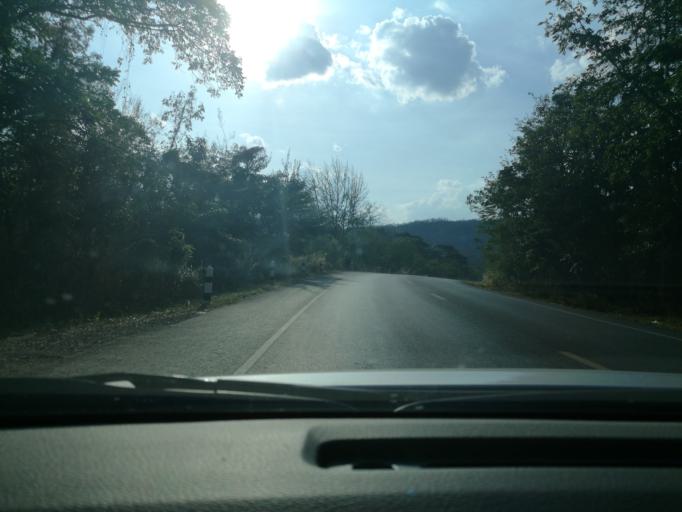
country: TH
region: Phetchabun
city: Phetchabun
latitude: 16.5462
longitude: 101.1214
